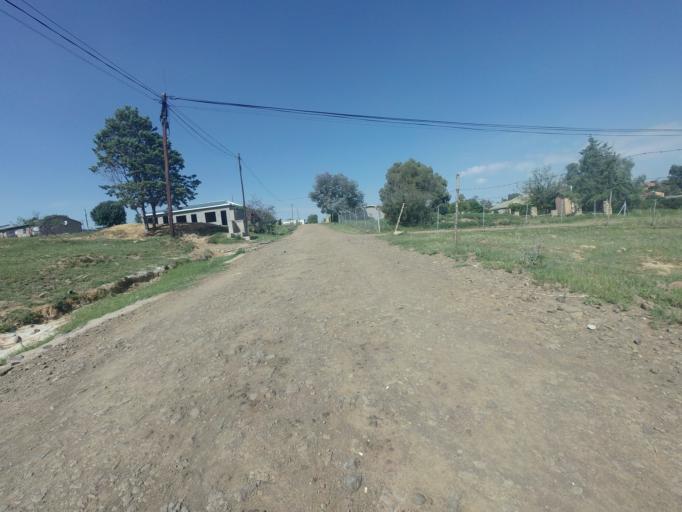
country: LS
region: Berea
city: Teyateyaneng
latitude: -29.1463
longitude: 27.7545
